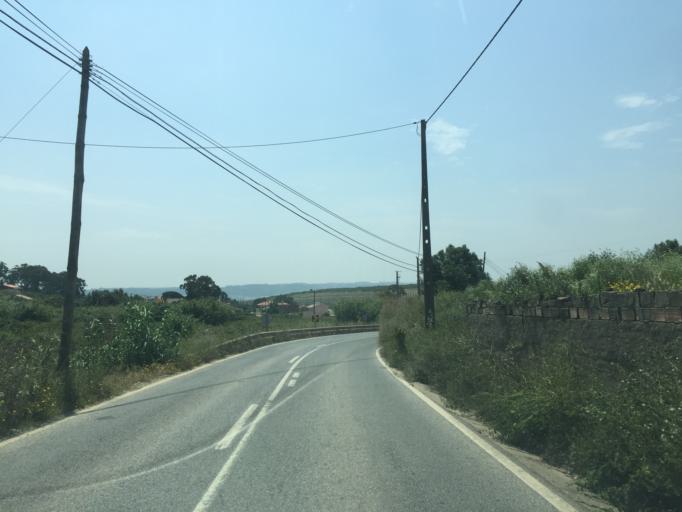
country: PT
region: Lisbon
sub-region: Loures
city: Loures
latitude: 38.8647
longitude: -9.1819
